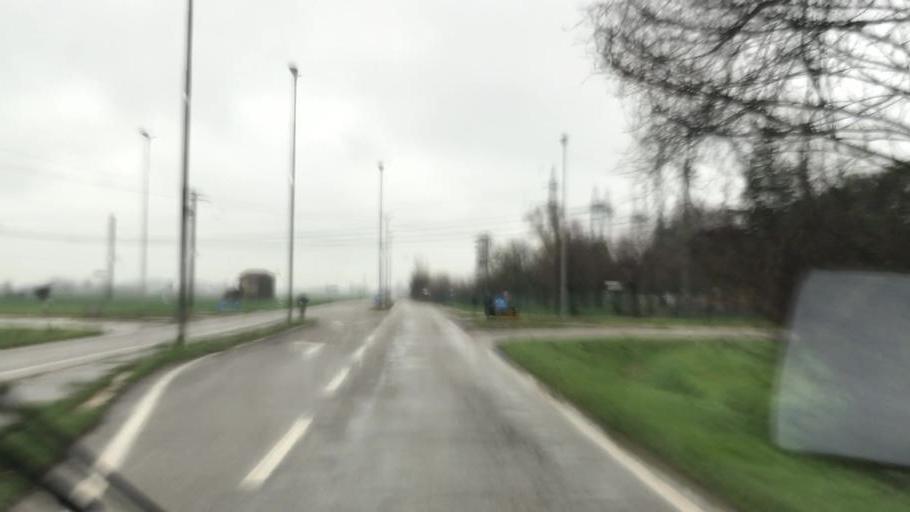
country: IT
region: Lombardy
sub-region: Provincia di Mantova
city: Carbonara di Po
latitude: 45.0209
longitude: 11.2522
